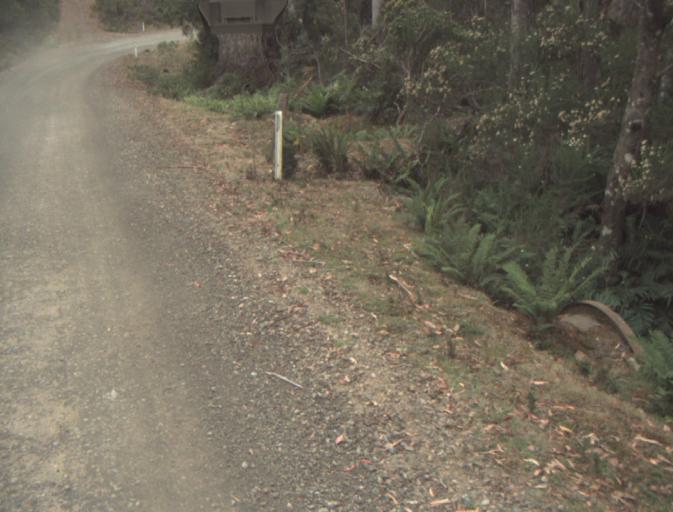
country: AU
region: Tasmania
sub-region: Dorset
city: Scottsdale
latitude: -41.4243
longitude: 147.5140
